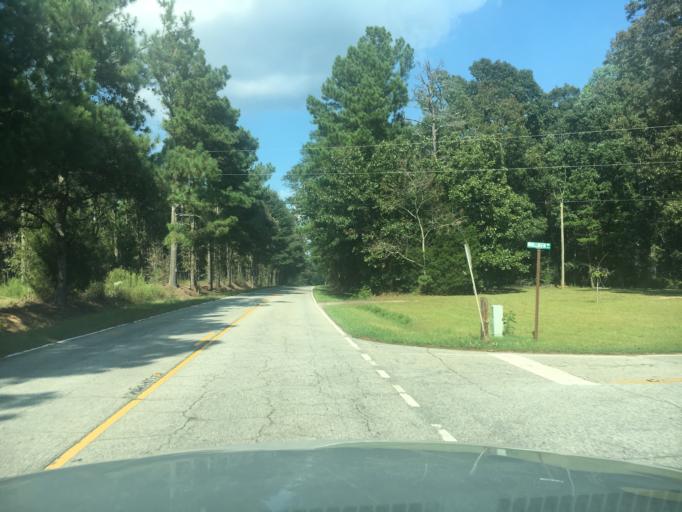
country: US
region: South Carolina
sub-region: Anderson County
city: Pendleton
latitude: 34.6753
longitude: -82.7571
